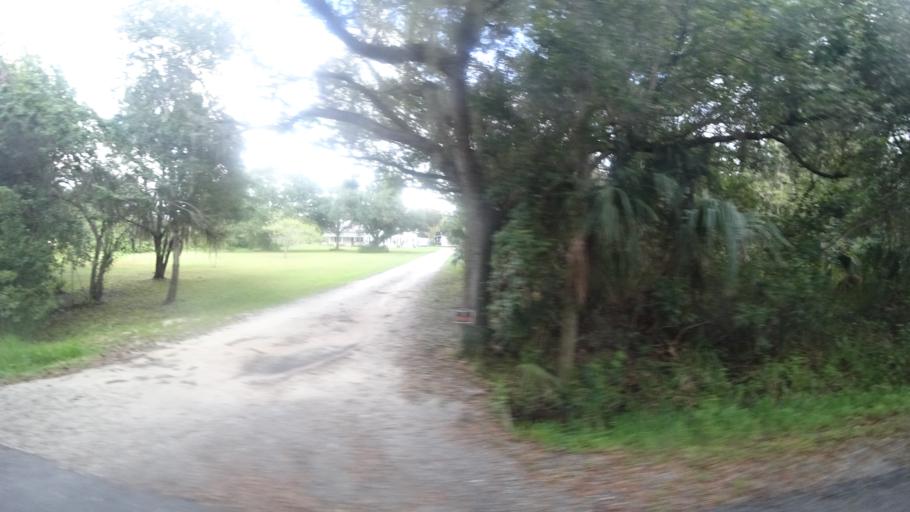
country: US
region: Florida
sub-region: Manatee County
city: Memphis
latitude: 27.6070
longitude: -82.5355
